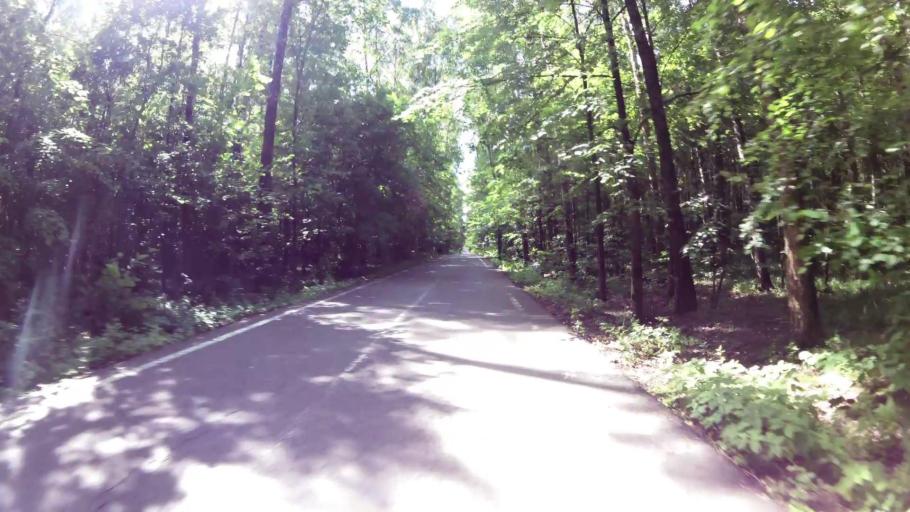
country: RU
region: Moscow
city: Babushkin
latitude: 55.8686
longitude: 37.7236
